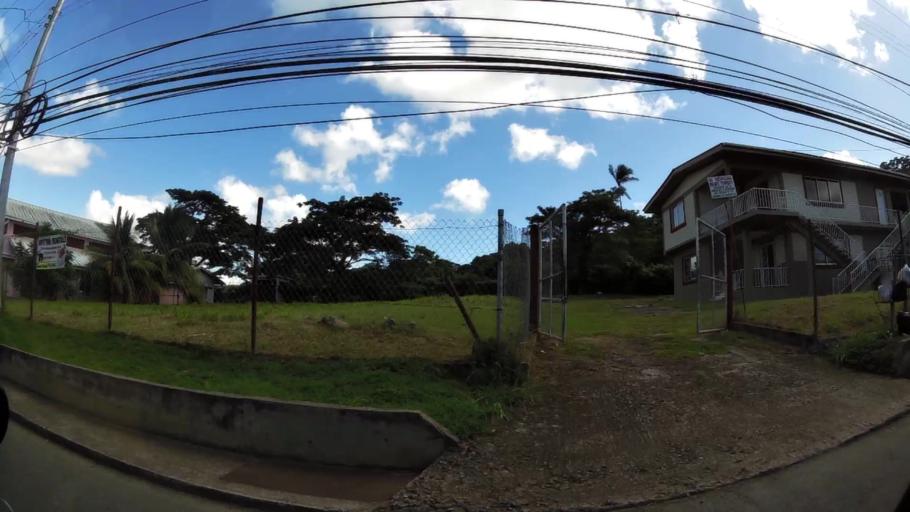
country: TT
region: Tobago
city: Scarborough
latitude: 11.2049
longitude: -60.7813
